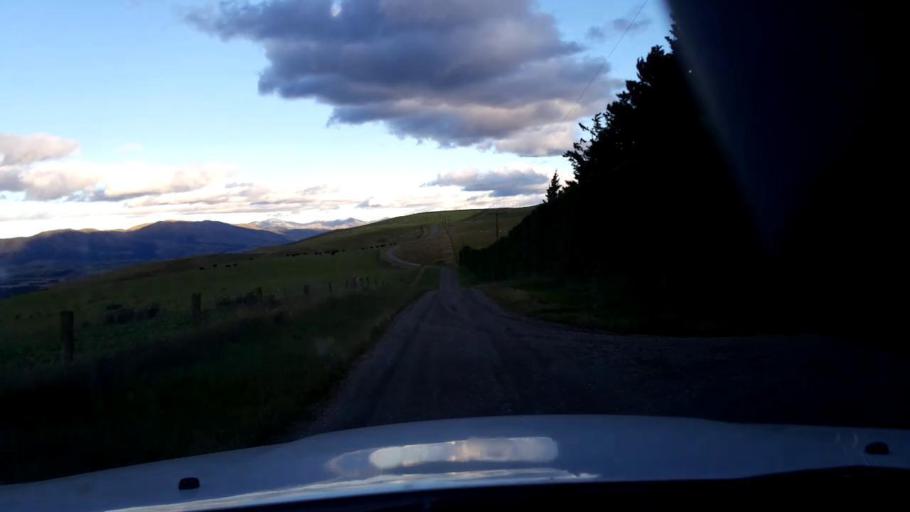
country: NZ
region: Canterbury
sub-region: Timaru District
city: Pleasant Point
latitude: -44.2559
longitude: 170.9131
